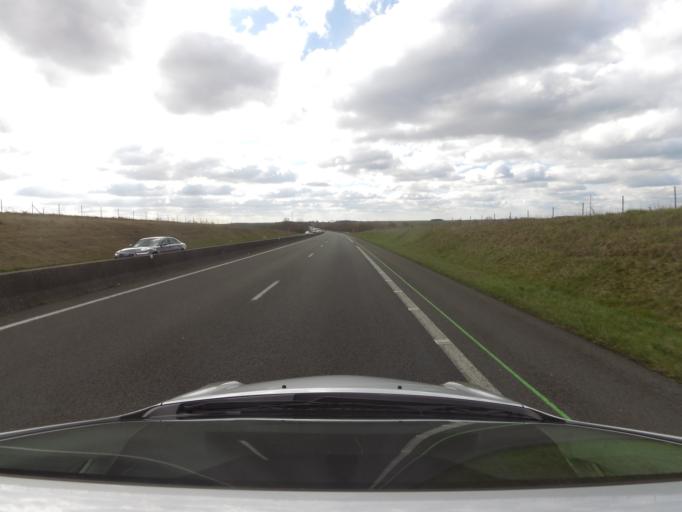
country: FR
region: Picardie
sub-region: Departement de la Somme
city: Nouvion
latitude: 50.2175
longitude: 1.7527
